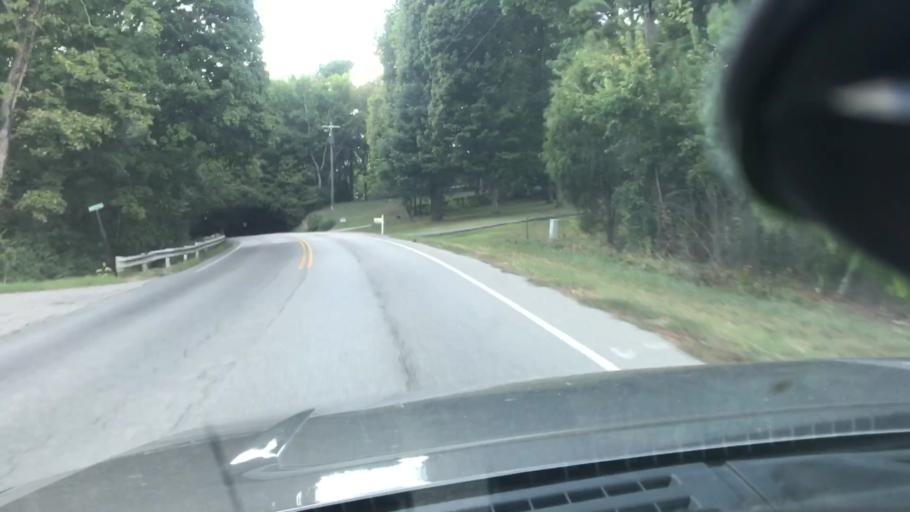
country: US
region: Tennessee
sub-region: Davidson County
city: Forest Hills
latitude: 36.0292
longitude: -86.9394
